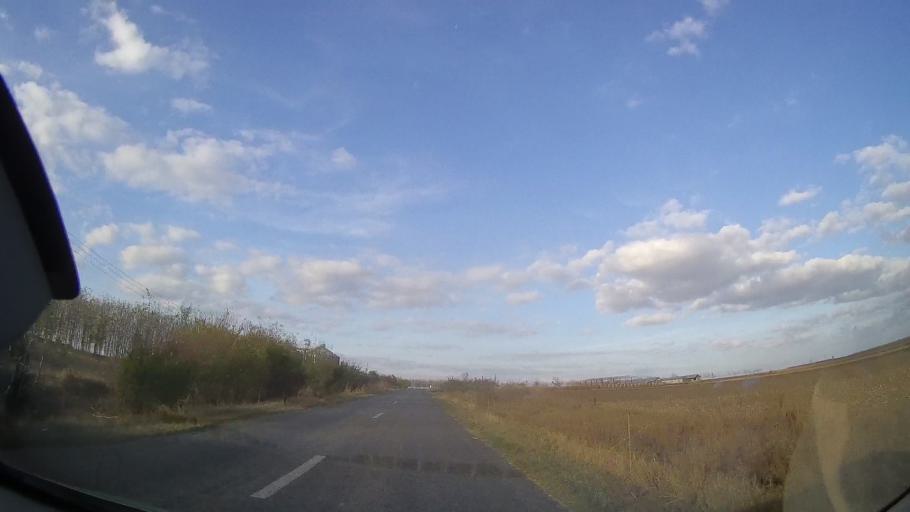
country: RO
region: Constanta
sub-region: Comuna Dumbraveni
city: Dumbraveni
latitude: 43.9246
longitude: 28.0296
